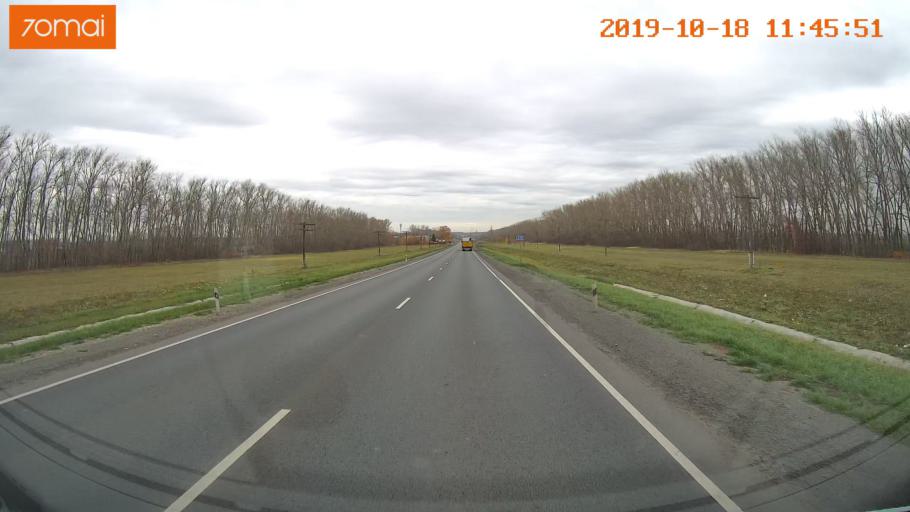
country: RU
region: Rjazan
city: Mikhaylov
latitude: 54.2142
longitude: 38.9757
